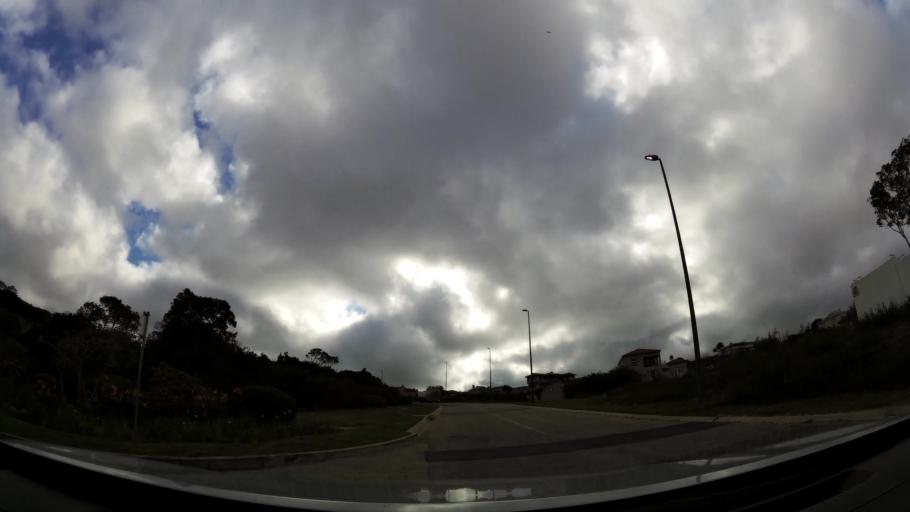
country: ZA
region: Western Cape
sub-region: Eden District Municipality
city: Plettenberg Bay
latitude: -34.0858
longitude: 23.3579
